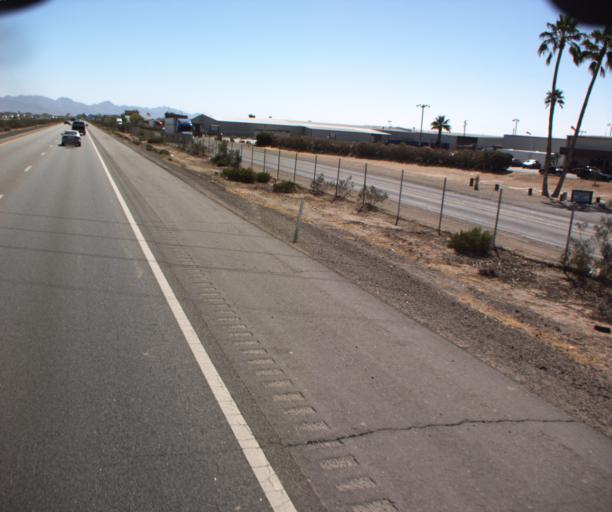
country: US
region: Arizona
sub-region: Yuma County
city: Yuma
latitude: 32.6813
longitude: -114.5550
